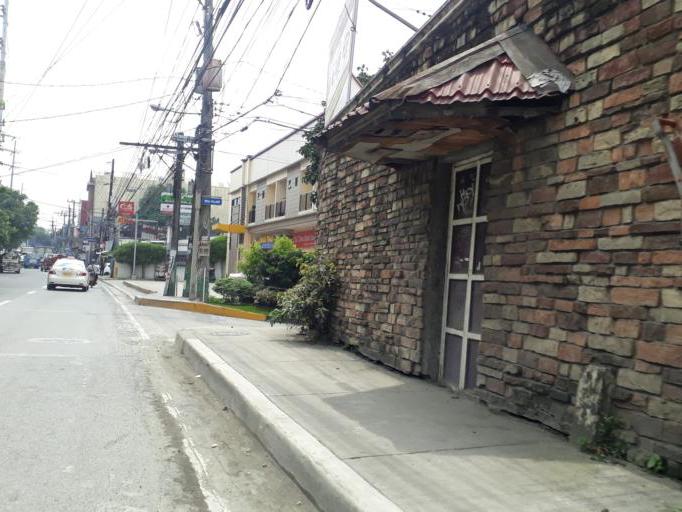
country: PH
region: Calabarzon
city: Bagong Pagasa
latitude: 14.6790
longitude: 121.0250
